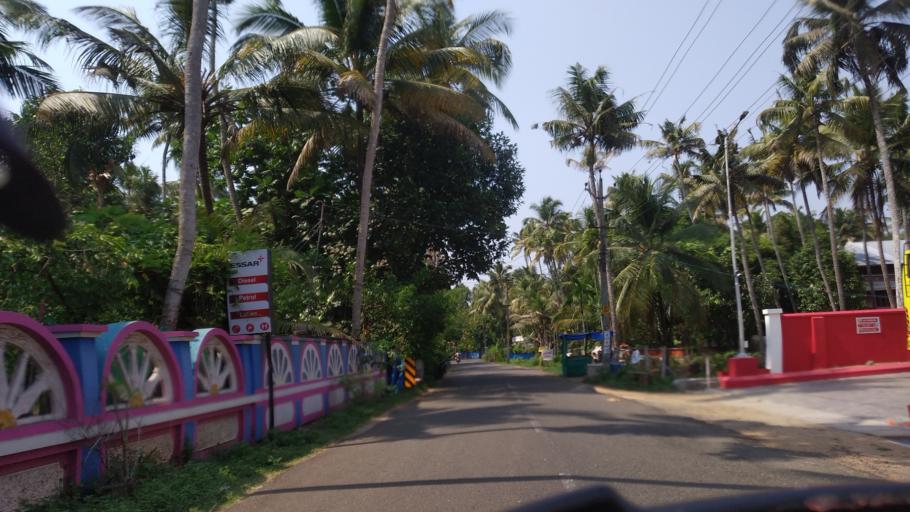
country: IN
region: Kerala
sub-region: Thrissur District
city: Irinjalakuda
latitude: 10.3208
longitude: 76.1246
